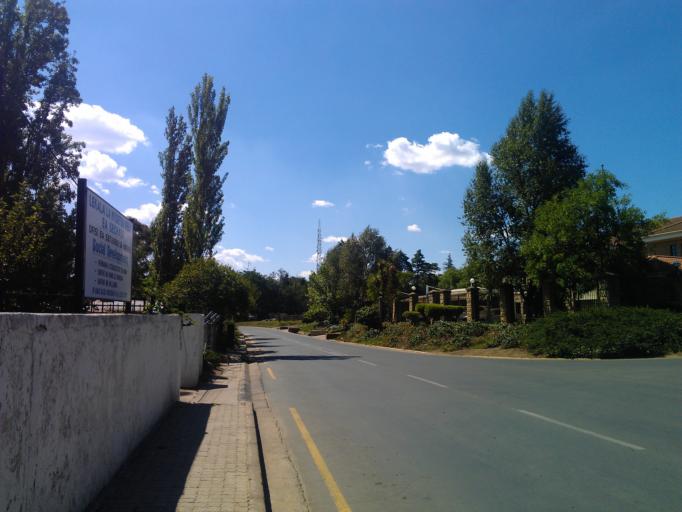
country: LS
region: Maseru
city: Maseru
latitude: -29.3095
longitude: 27.4778
